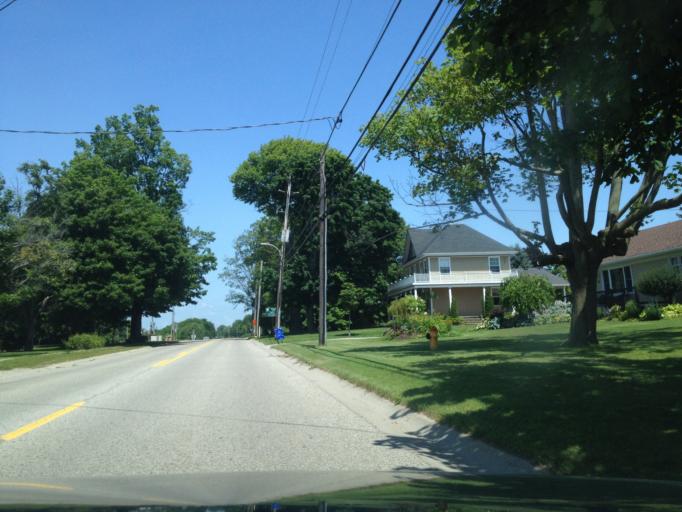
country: CA
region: Ontario
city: Aylmer
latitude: 42.6509
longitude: -80.8002
